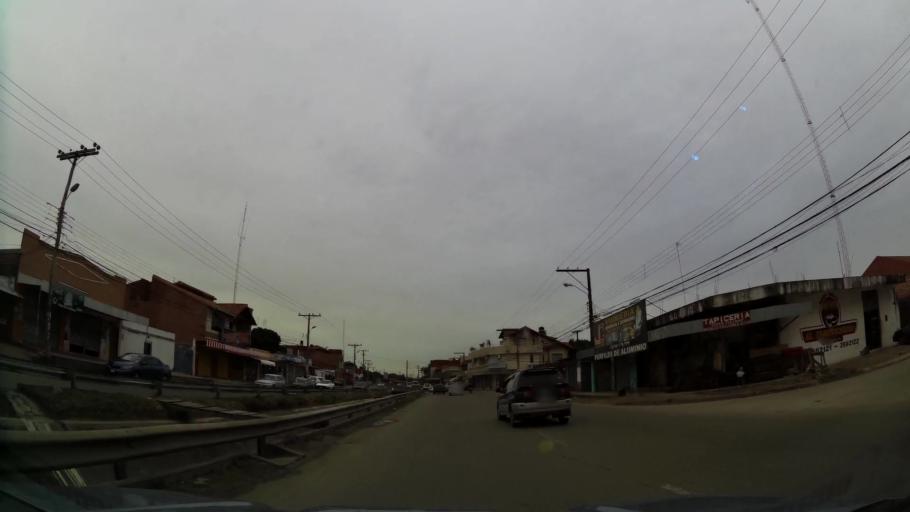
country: BO
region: Santa Cruz
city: Santa Cruz de la Sierra
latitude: -17.8149
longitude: -63.1772
